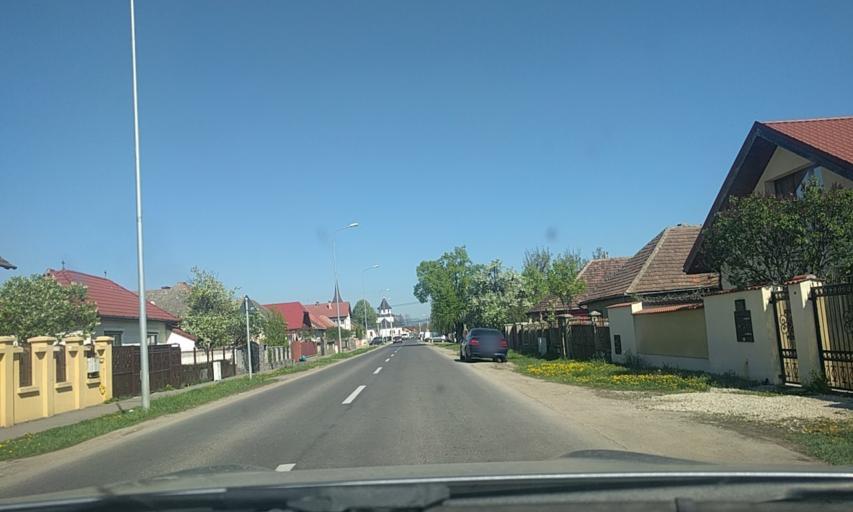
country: RO
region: Brasov
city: Brasov
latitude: 45.6966
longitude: 25.5597
